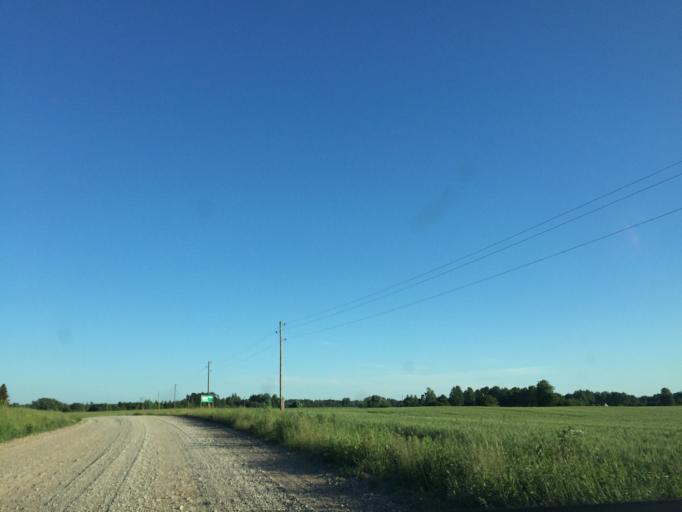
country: LV
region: Broceni
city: Broceni
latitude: 56.7962
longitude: 22.5510
